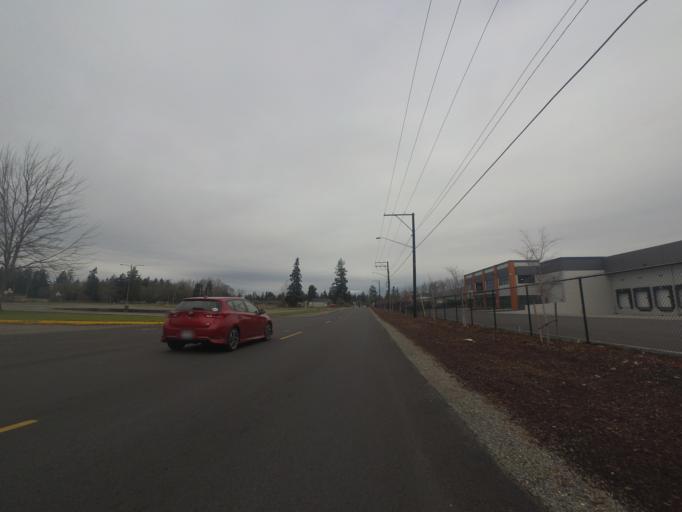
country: US
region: Washington
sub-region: Pierce County
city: Fort Lewis
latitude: 47.1223
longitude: -122.5374
